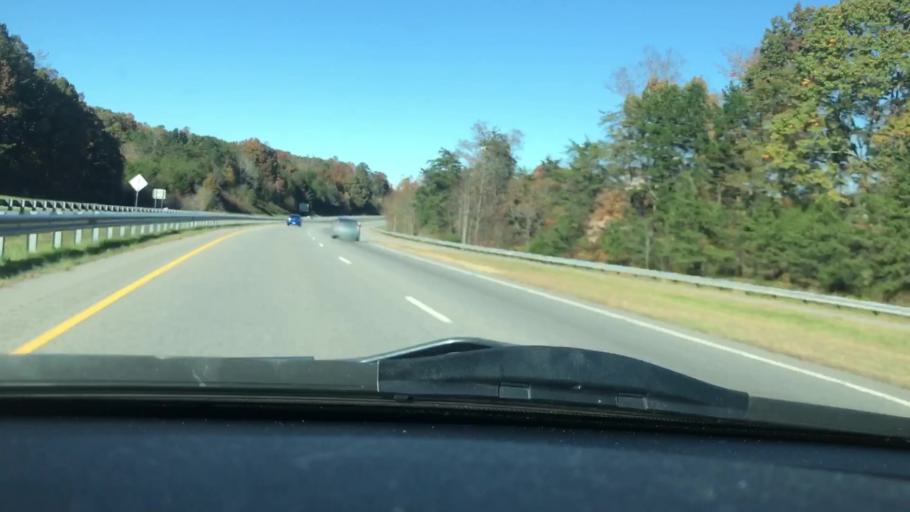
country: US
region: North Carolina
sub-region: Rockingham County
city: Stoneville
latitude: 36.4688
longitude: -79.9266
